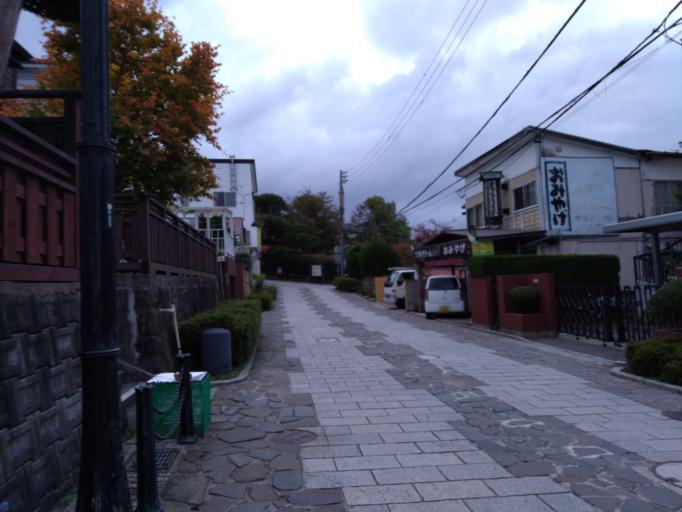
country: JP
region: Hokkaido
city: Hakodate
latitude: 41.7644
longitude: 140.7104
